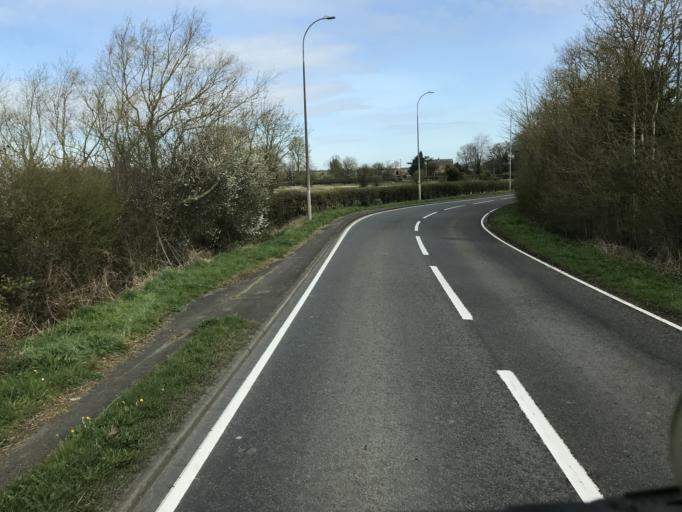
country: GB
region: England
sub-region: Lincolnshire
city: Market Rasen
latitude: 53.3874
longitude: -0.4010
